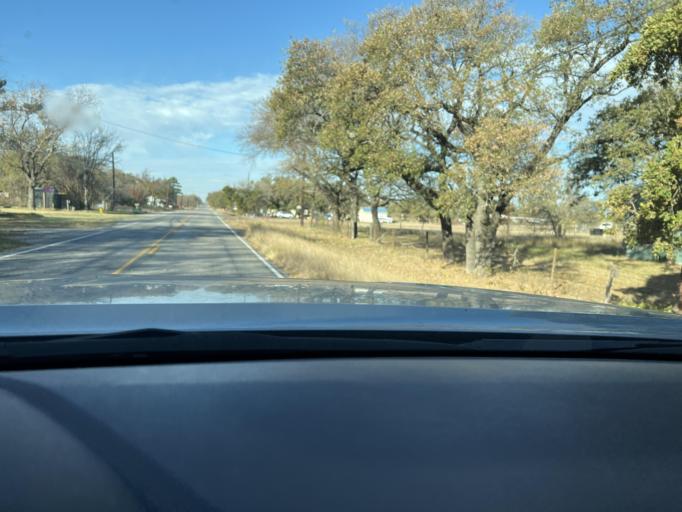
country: US
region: Texas
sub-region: Eastland County
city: Eastland
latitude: 32.4193
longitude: -98.7435
